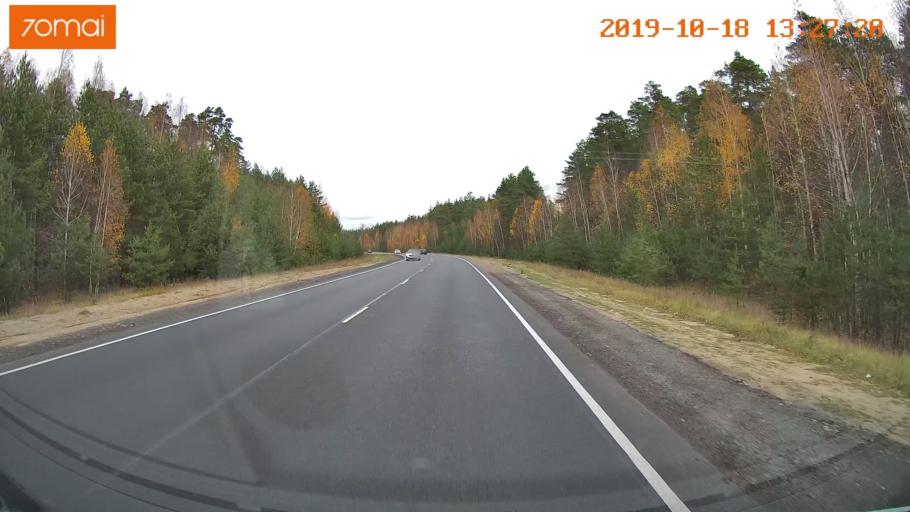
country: RU
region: Rjazan
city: Solotcha
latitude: 54.7626
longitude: 39.8529
